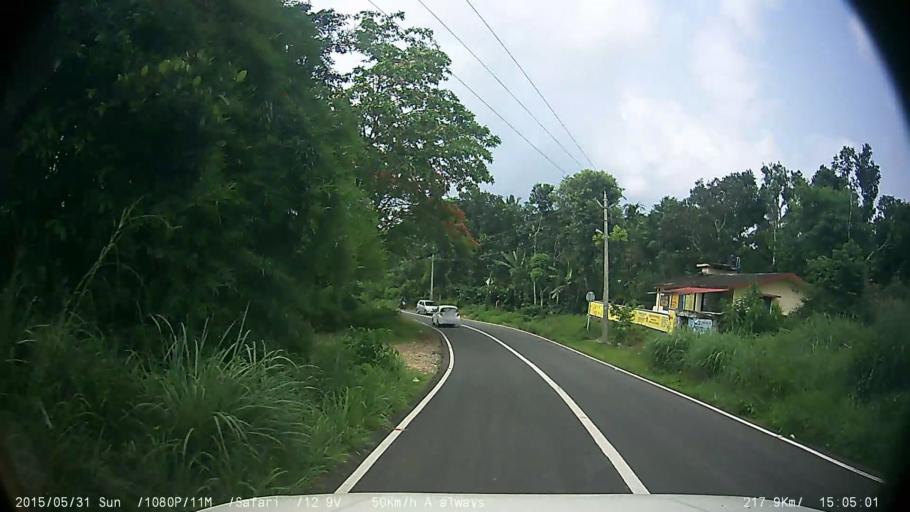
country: IN
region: Kerala
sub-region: Wayanad
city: Kalpetta
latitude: 11.6365
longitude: 76.2129
